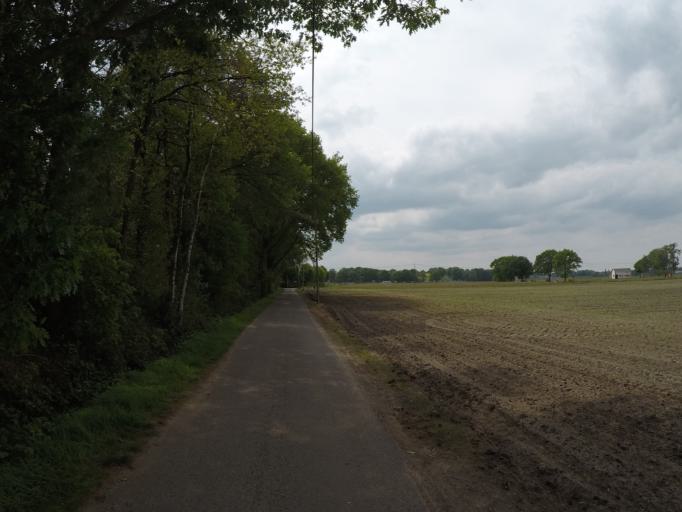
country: BE
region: Flanders
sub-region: Provincie Antwerpen
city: Zoersel
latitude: 51.2770
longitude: 4.6968
